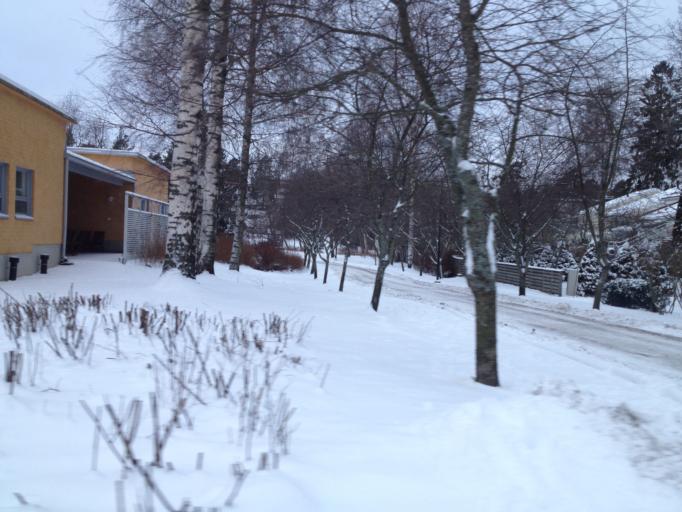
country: FI
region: Uusimaa
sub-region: Helsinki
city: Vantaa
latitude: 60.2013
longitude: 25.0795
